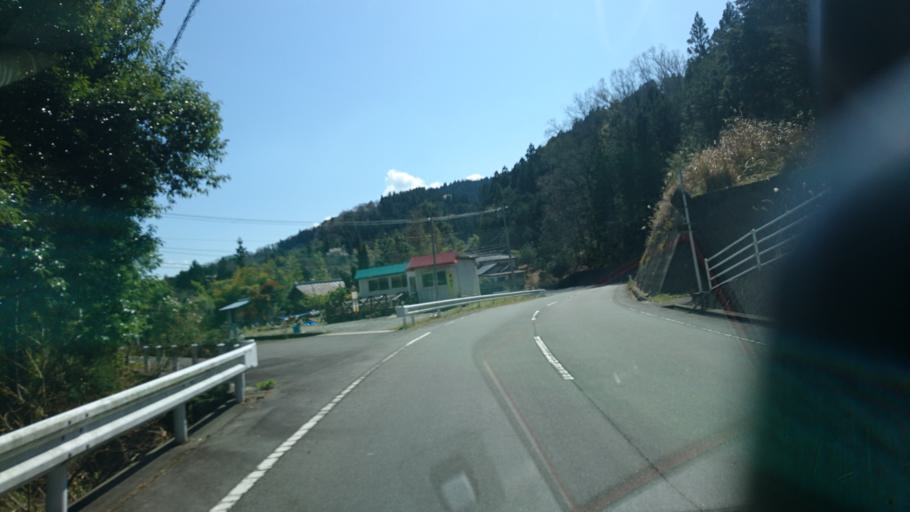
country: JP
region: Shizuoka
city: Fujinomiya
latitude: 35.3447
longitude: 138.4388
